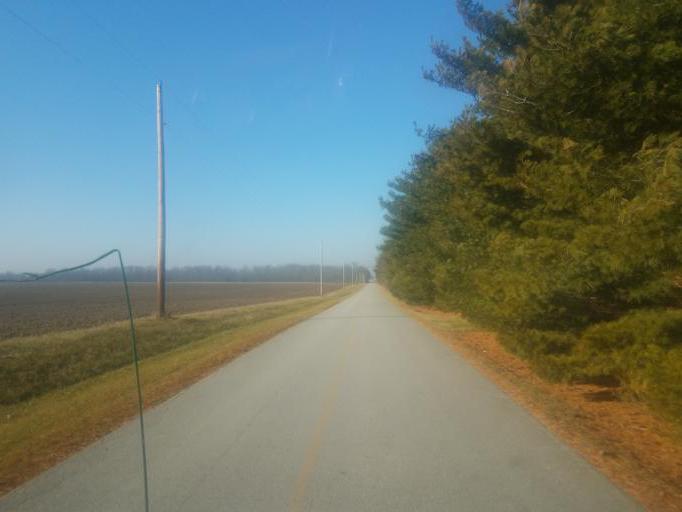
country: US
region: Ohio
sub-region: Crawford County
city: Bucyrus
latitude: 41.0373
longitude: -82.9589
